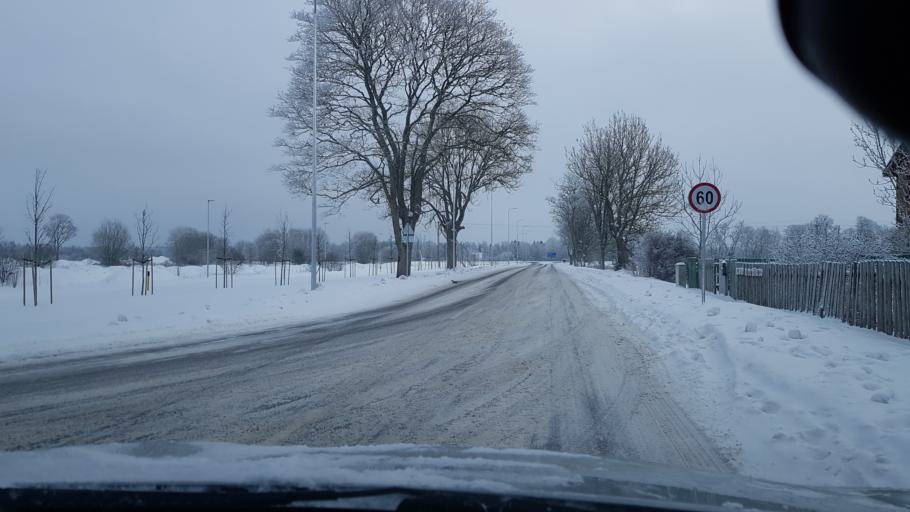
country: EE
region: Harju
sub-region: Keila linn
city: Keila
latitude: 59.3225
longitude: 24.4539
